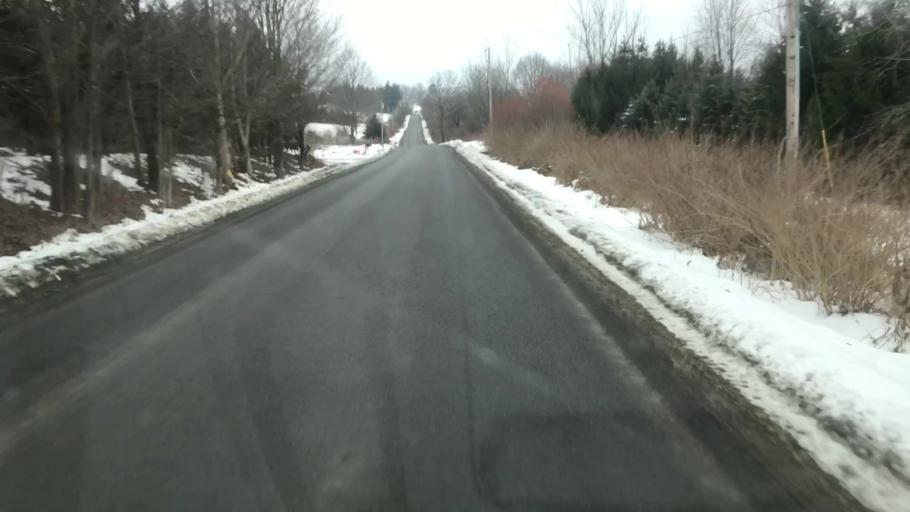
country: US
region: New York
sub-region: Cortland County
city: Cortland West
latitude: 42.6503
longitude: -76.2660
